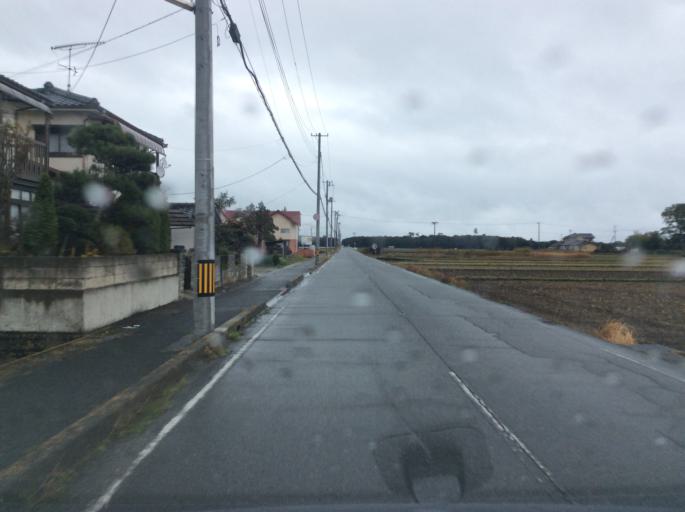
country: JP
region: Fukushima
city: Iwaki
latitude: 37.0679
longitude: 140.9593
